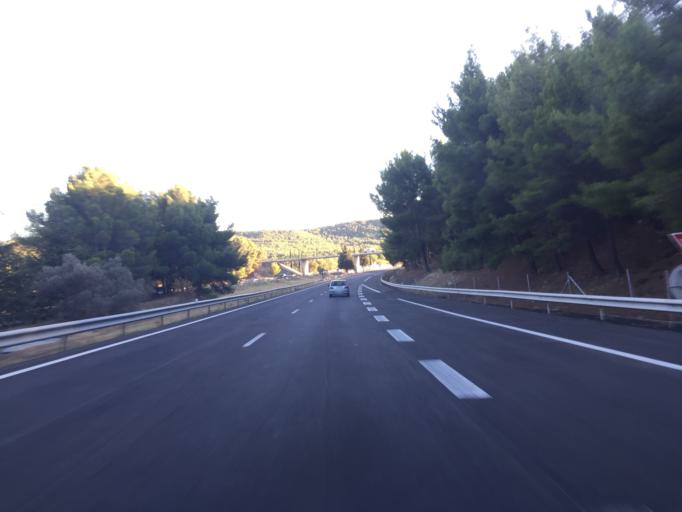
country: FR
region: Provence-Alpes-Cote d'Azur
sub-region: Departement des Bouches-du-Rhone
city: Coudoux
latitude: 43.5525
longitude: 5.2309
